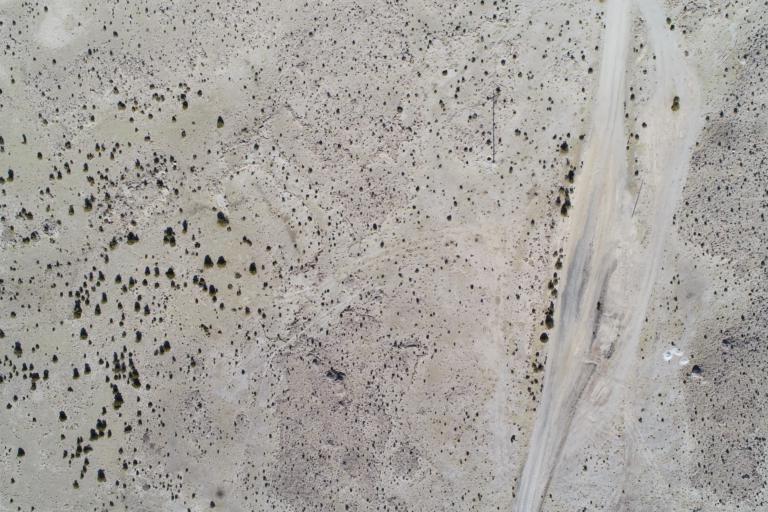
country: BO
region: Potosi
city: Colchani
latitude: -20.3520
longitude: -66.8949
